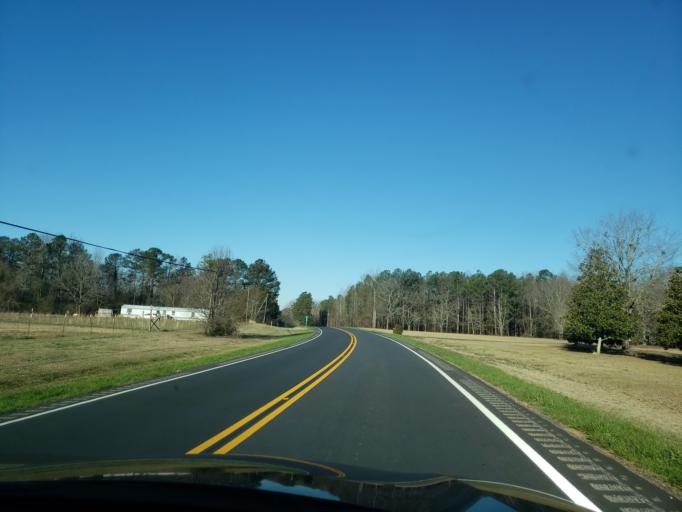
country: US
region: Alabama
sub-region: Macon County
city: Tuskegee
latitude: 32.5818
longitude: -85.7174
